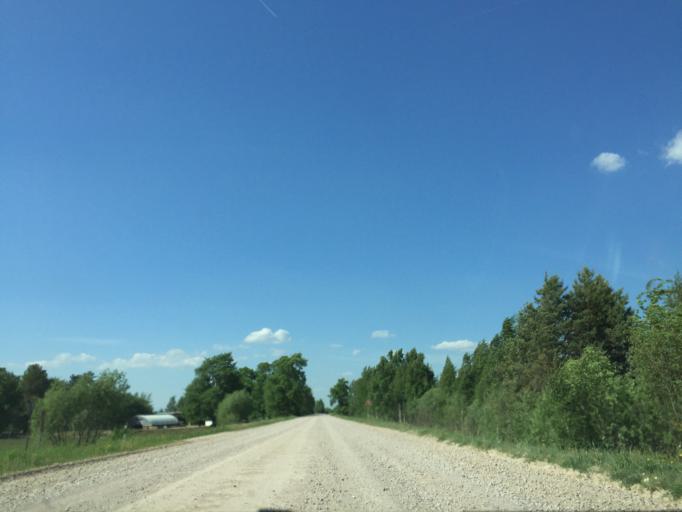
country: LV
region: Rundales
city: Pilsrundale
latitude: 56.5450
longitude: 23.9905
